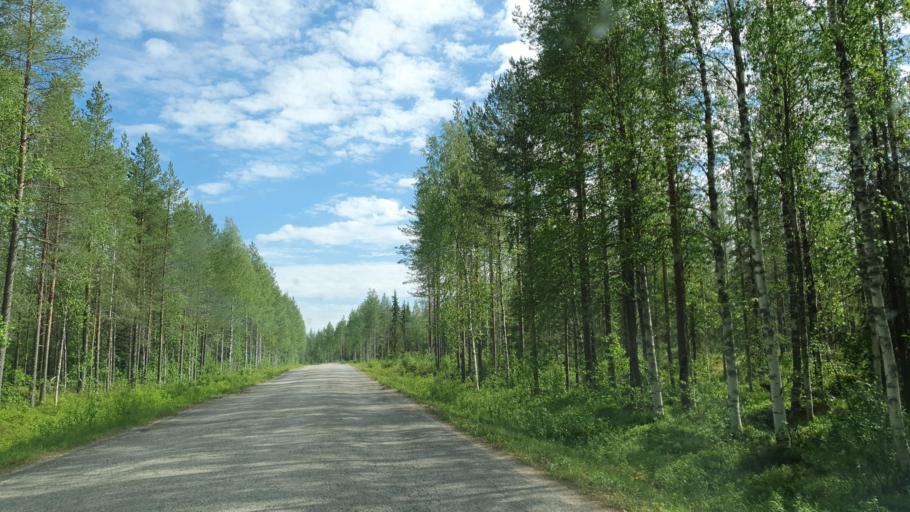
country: FI
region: Kainuu
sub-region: Kehys-Kainuu
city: Kuhmo
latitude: 64.5226
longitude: 29.3786
